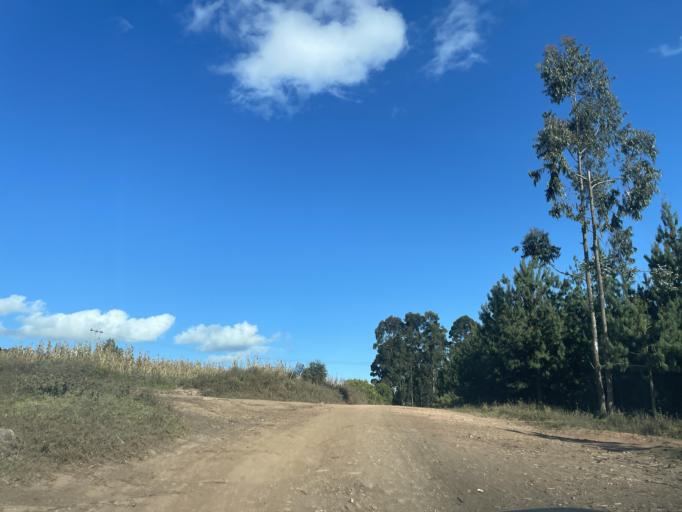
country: TZ
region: Iringa
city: Makungu
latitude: -8.5010
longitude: 35.5091
